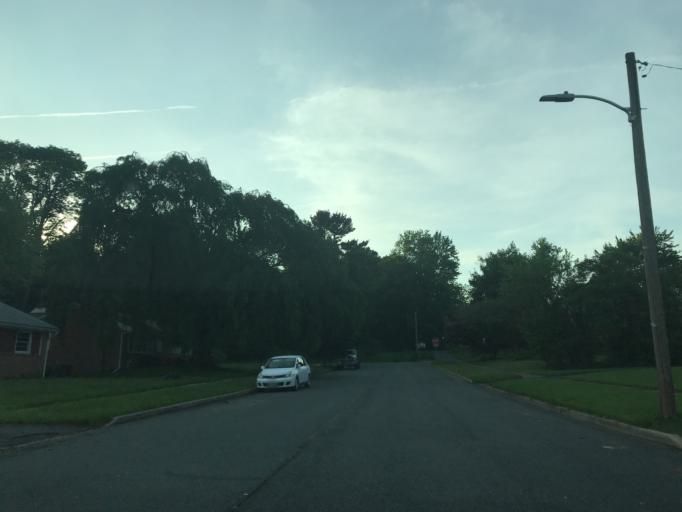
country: US
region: Maryland
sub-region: Harford County
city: North Bel Air
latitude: 39.5332
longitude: -76.3571
